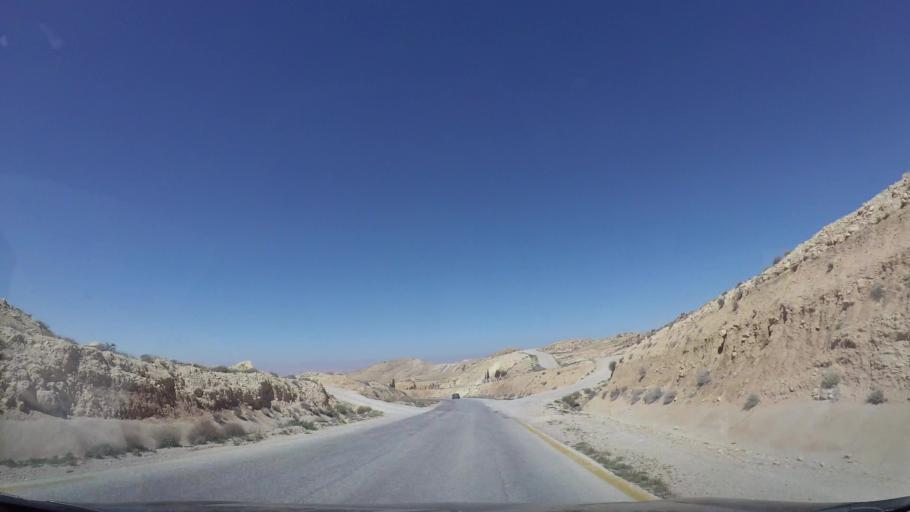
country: JO
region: Tafielah
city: At Tafilah
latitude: 30.8522
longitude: 35.5551
